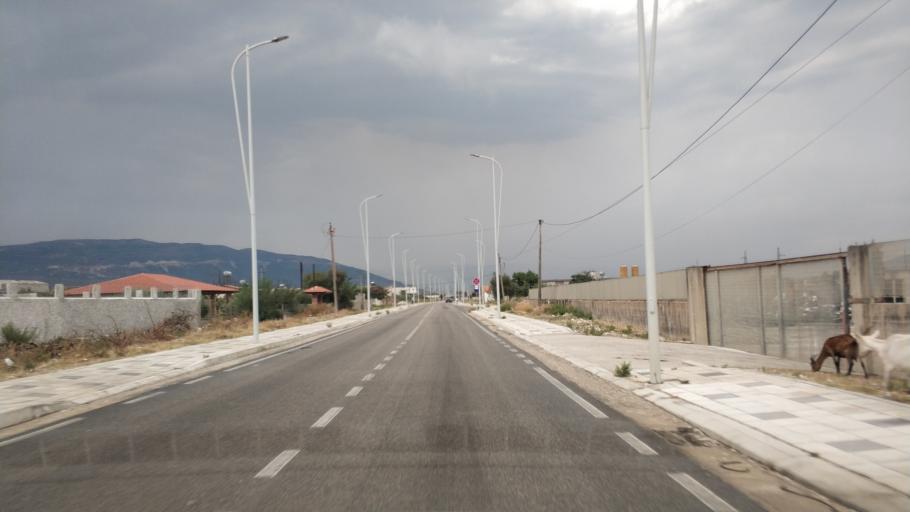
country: AL
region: Vlore
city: Vlore
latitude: 40.4802
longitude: 19.4668
